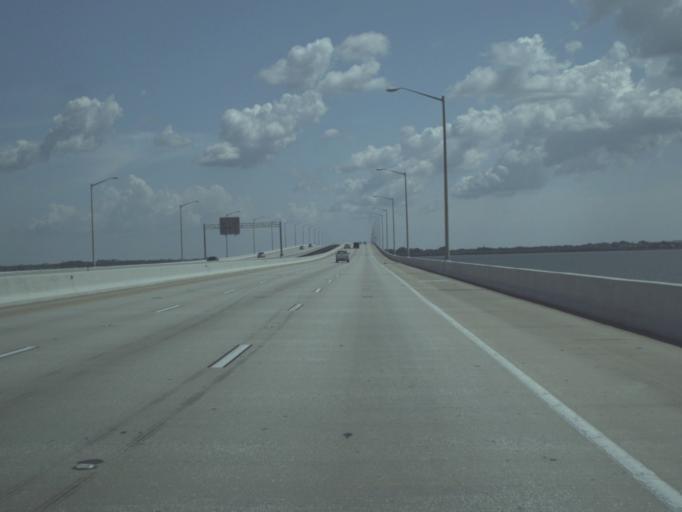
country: US
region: Florida
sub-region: Pinellas County
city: South Highpoint
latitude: 27.9512
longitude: -82.7069
